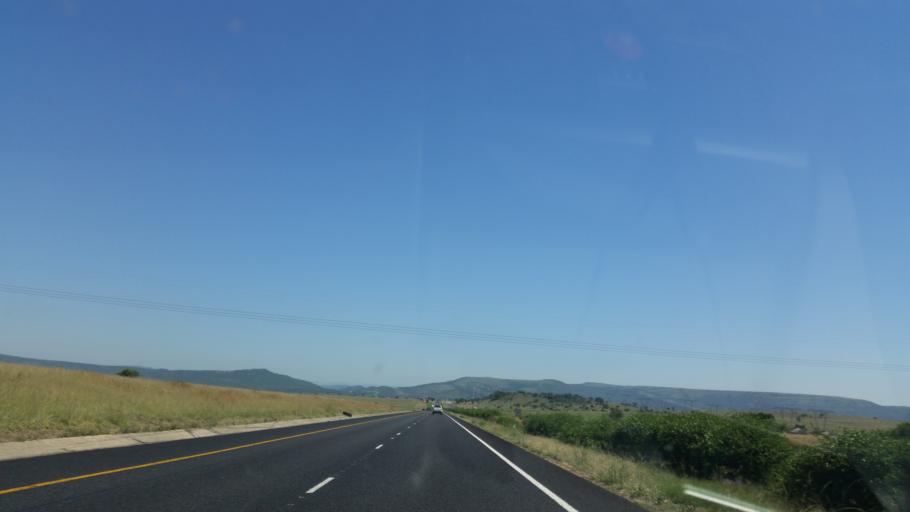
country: ZA
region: KwaZulu-Natal
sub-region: uThukela District Municipality
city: Ladysmith
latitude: -28.8010
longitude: 29.6885
